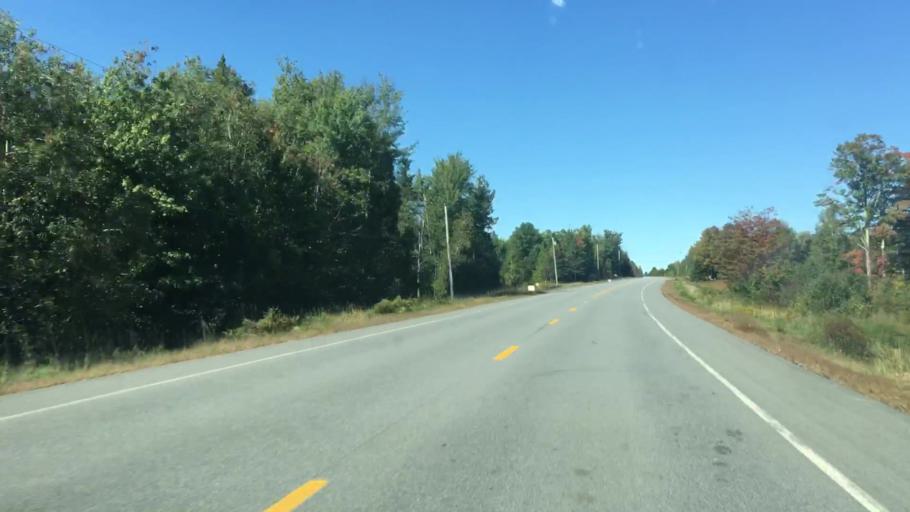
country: US
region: Maine
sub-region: Piscataquis County
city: Sangerville
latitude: 45.0696
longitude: -69.4589
